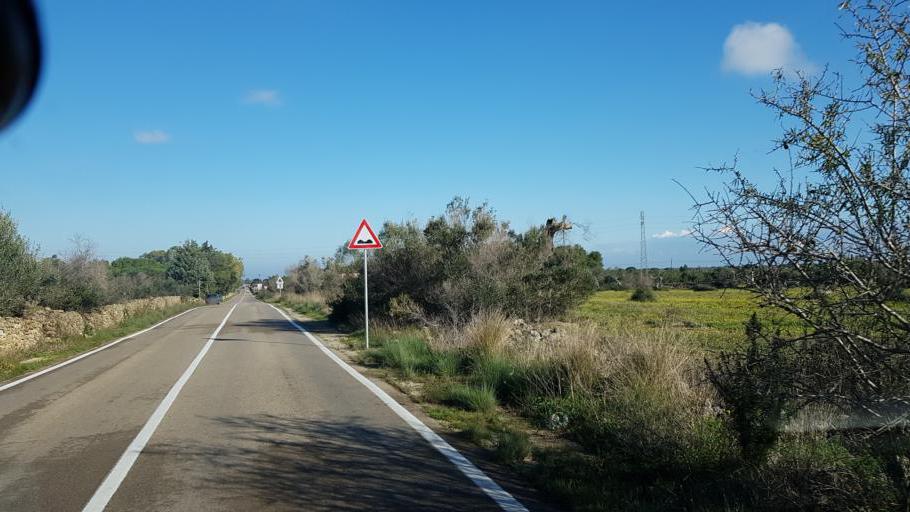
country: IT
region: Apulia
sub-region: Provincia di Lecce
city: Trepuzzi
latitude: 40.4557
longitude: 18.1131
